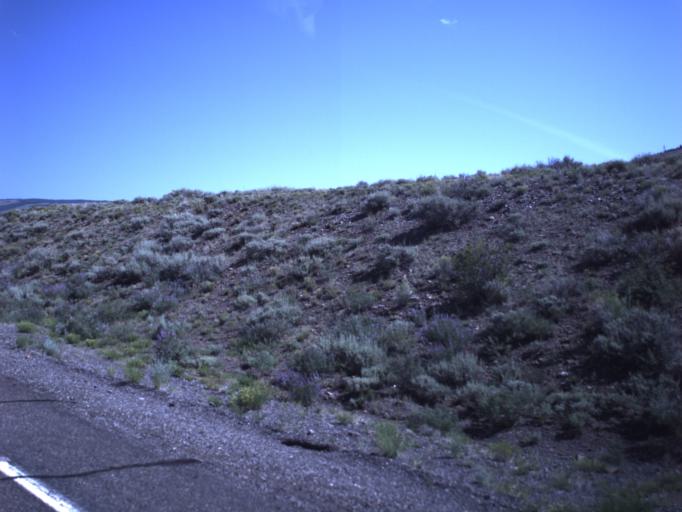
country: US
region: Utah
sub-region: Wayne County
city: Loa
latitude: 38.5448
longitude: -111.5112
